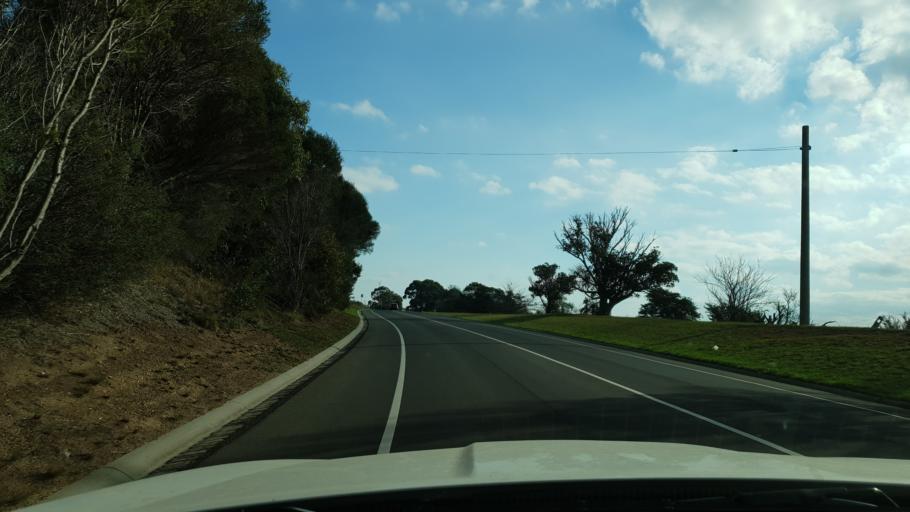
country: AU
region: Victoria
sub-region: East Gippsland
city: Bairnsdale
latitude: -37.8166
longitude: 147.6120
